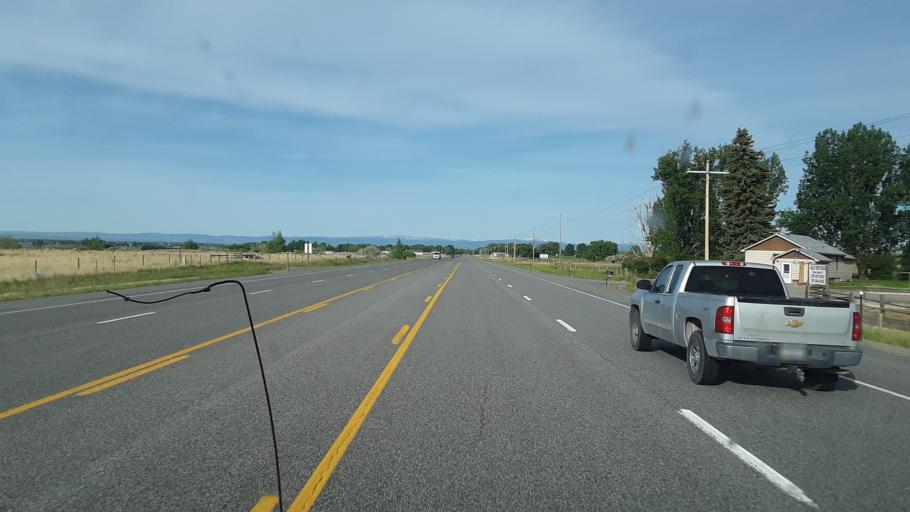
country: US
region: Wyoming
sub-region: Fremont County
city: Riverton
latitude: 43.1157
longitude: -108.3309
